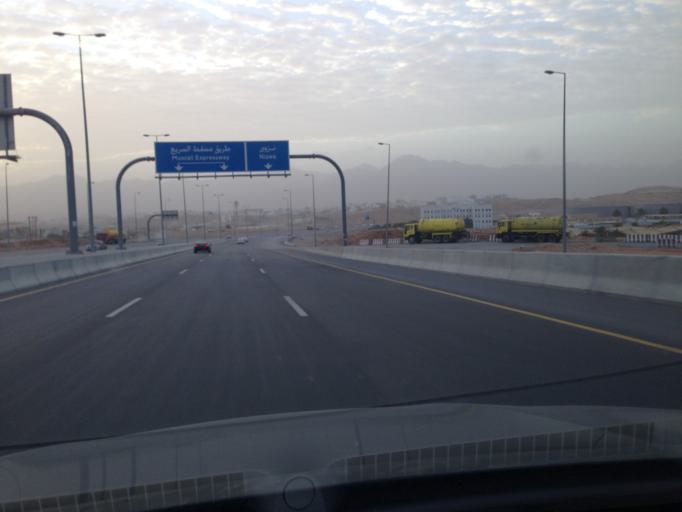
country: OM
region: Muhafazat Masqat
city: Bawshar
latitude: 23.5689
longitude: 58.3346
